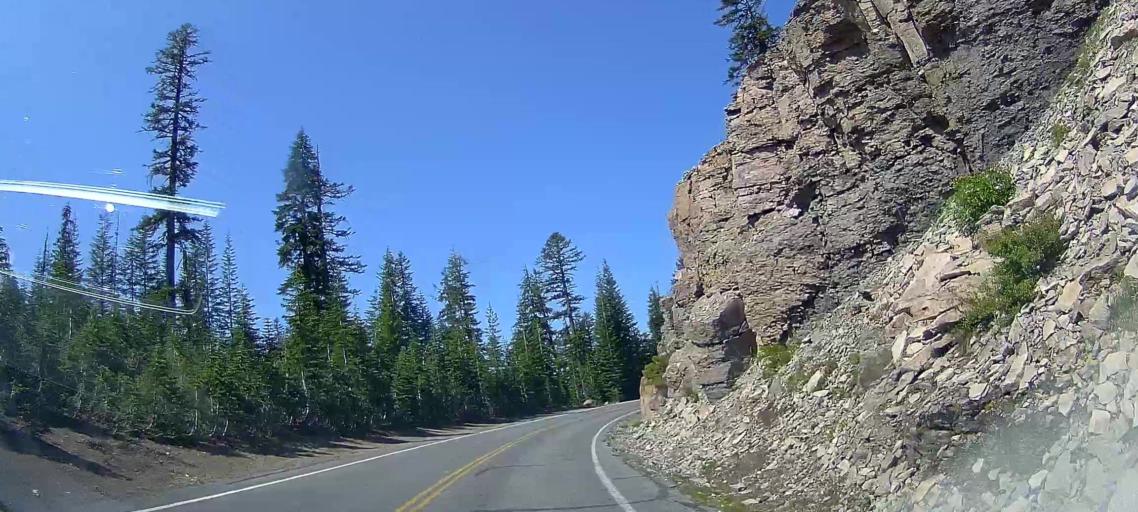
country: US
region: Oregon
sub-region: Klamath County
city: Klamath Falls
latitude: 42.8765
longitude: -122.1047
